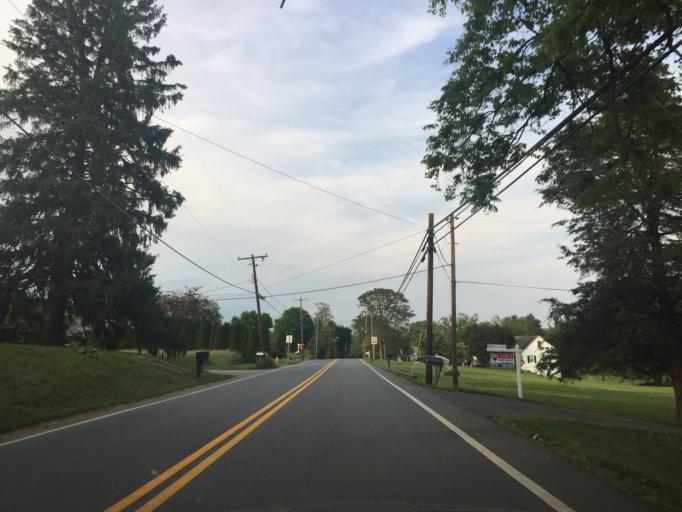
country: US
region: Maryland
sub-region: Frederick County
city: Brunswick
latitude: 39.3323
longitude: -77.6181
